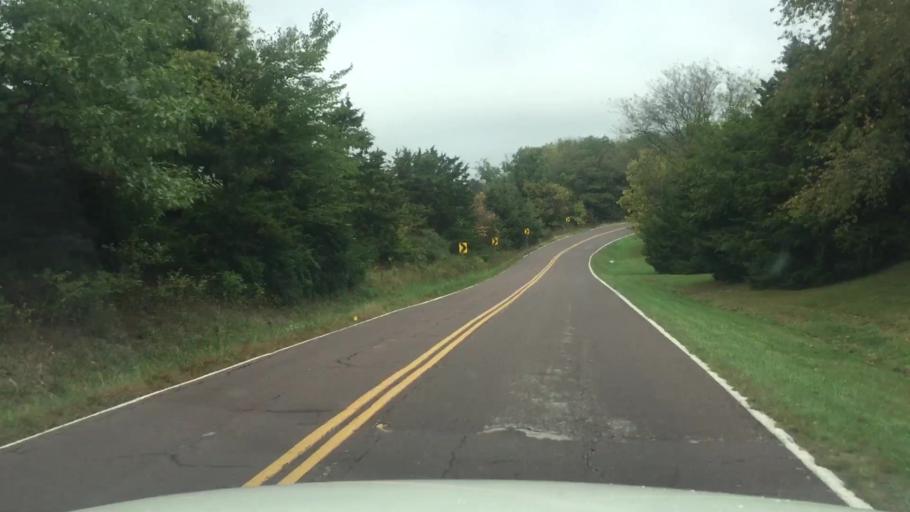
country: US
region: Missouri
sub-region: Boone County
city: Columbia
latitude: 38.8460
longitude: -92.3371
